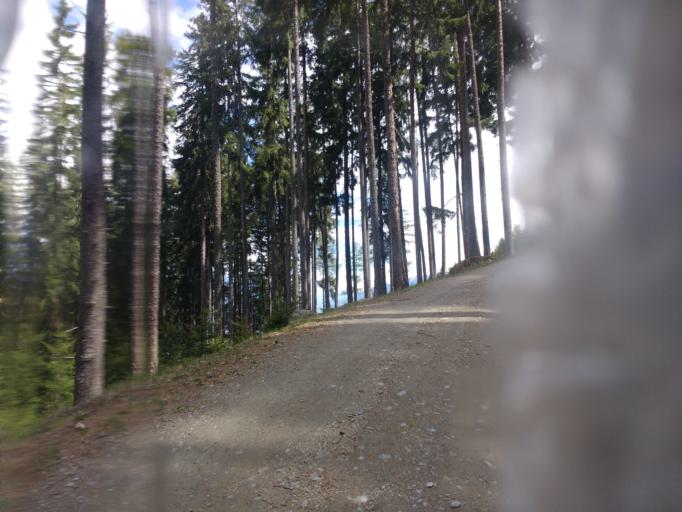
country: AT
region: Tyrol
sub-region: Politischer Bezirk Innsbruck Land
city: Rinn
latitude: 47.2394
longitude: 11.4931
